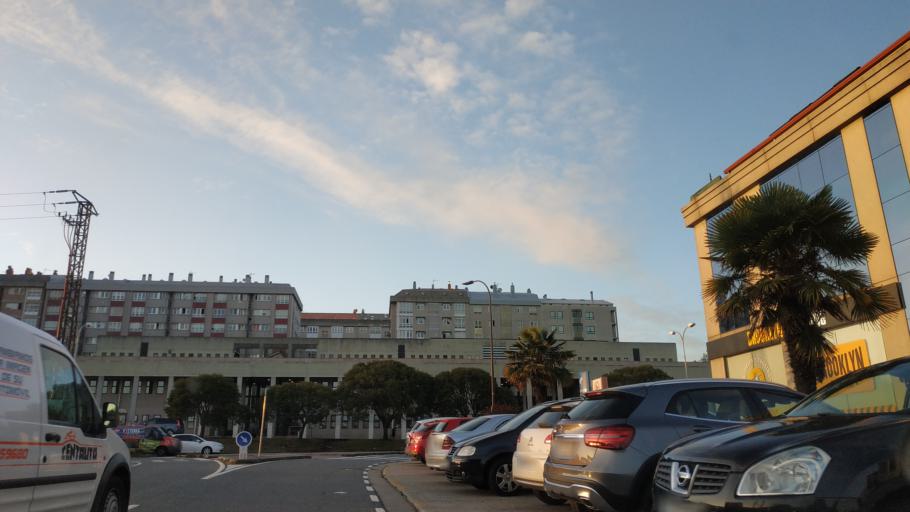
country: ES
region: Galicia
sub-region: Provincia da Coruna
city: A Coruna
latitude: 43.3574
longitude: -8.4224
